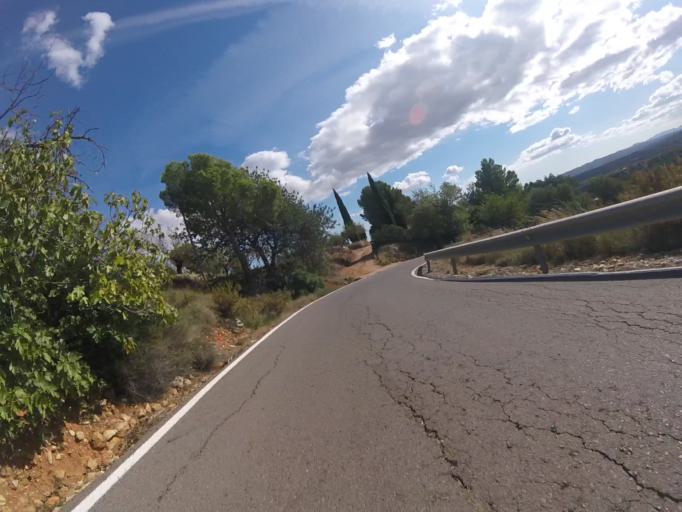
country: ES
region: Valencia
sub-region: Provincia de Castello
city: Cuevas de Vinroma
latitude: 40.3767
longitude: 0.1130
